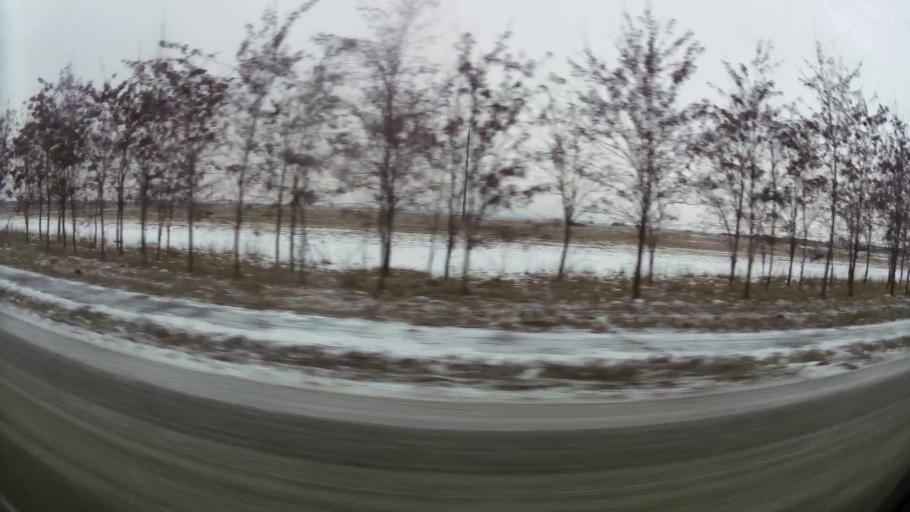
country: RO
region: Prahova
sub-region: Comuna Berceni
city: Corlatesti
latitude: 44.9226
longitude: 26.0763
